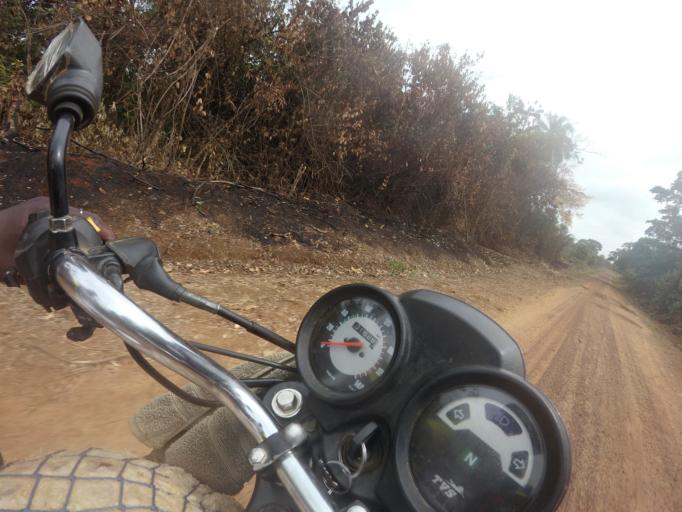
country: SL
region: Southern Province
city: Zimmi
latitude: 7.1673
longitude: -11.2383
